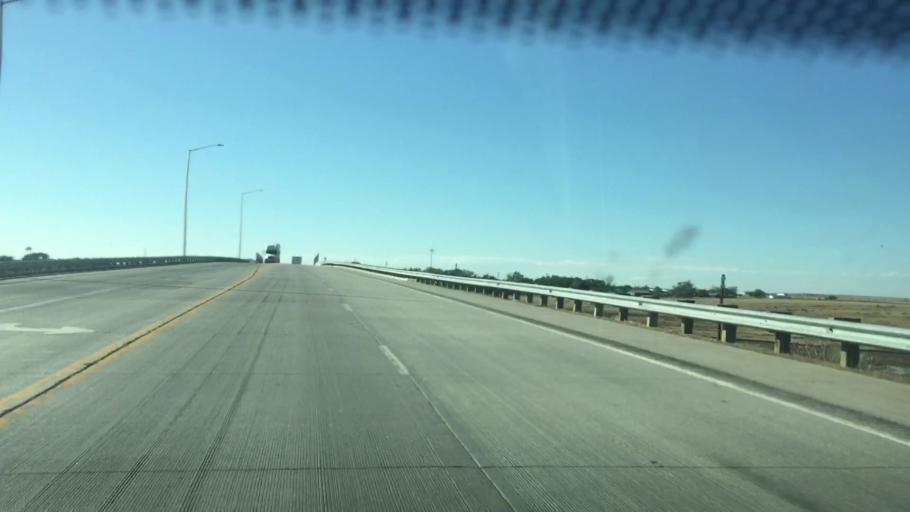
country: US
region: Colorado
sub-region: Kiowa County
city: Eads
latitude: 38.7629
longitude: -102.7810
